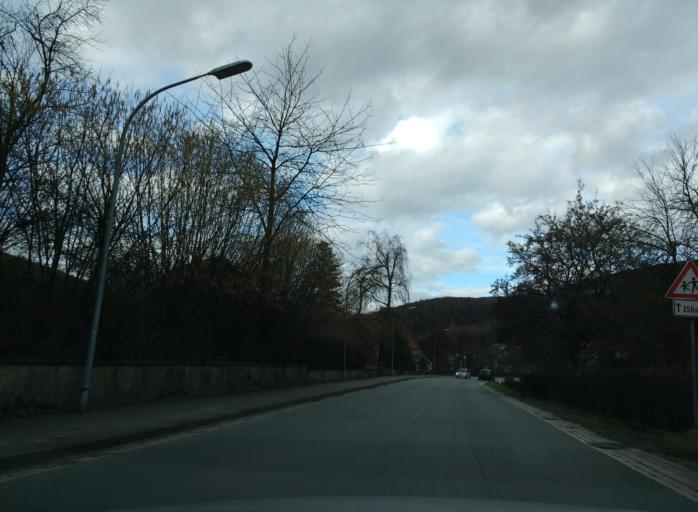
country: DE
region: North Rhine-Westphalia
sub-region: Regierungsbezirk Detmold
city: Dorentrup
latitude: 52.1104
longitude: 8.9529
